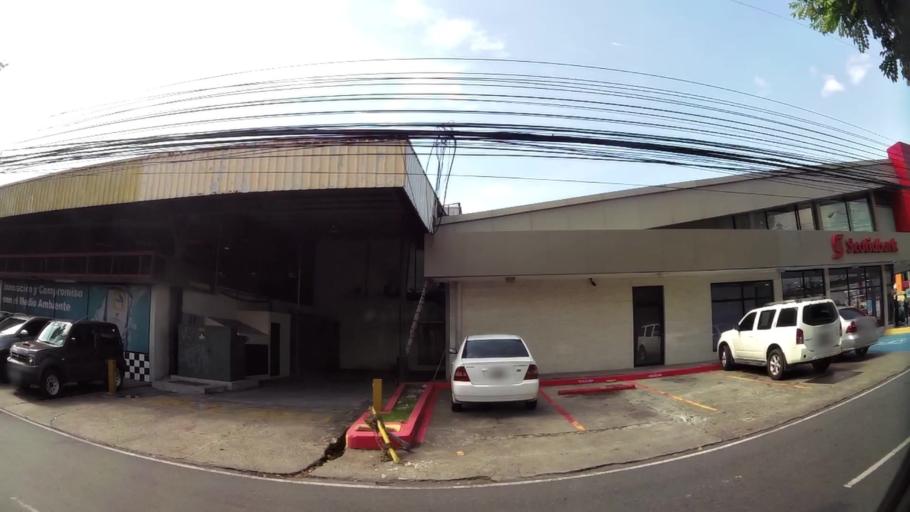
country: PA
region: Panama
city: Panama
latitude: 8.9979
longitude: -79.5257
